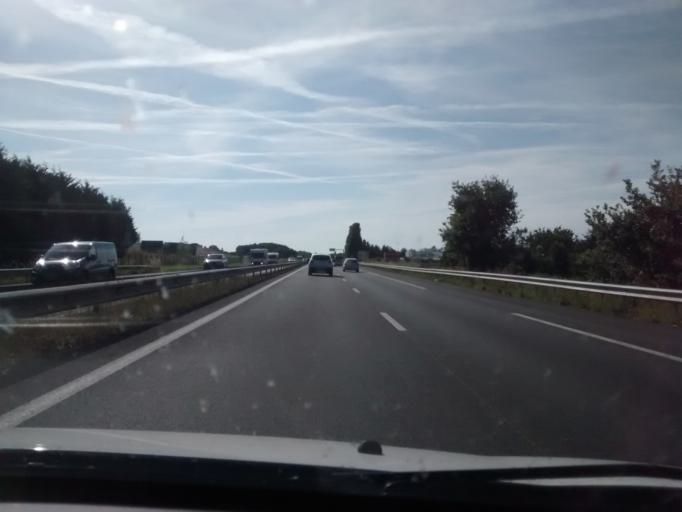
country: FR
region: Brittany
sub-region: Departement d'Ille-et-Vilaine
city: Chateaubourg
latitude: 48.0976
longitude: -1.4105
